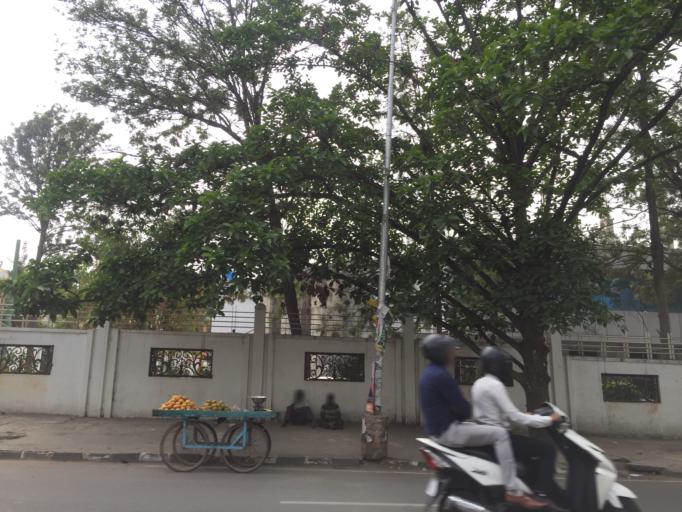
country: IN
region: Karnataka
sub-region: Bangalore Urban
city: Bangalore
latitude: 13.0213
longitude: 77.6433
